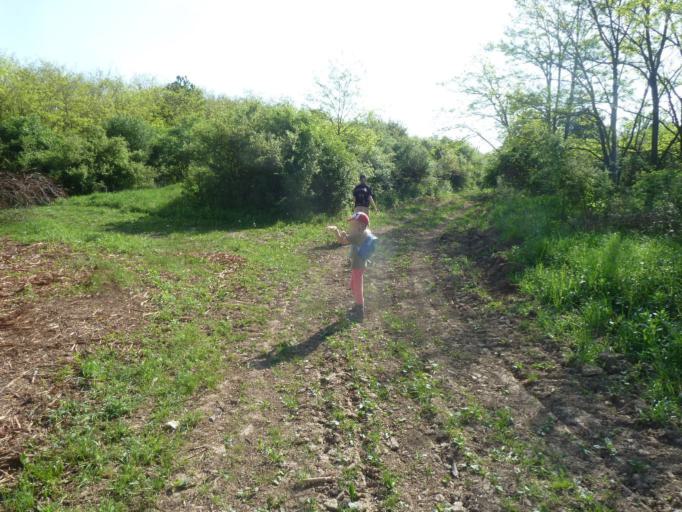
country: HU
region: Borsod-Abauj-Zemplen
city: Encs
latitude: 48.4233
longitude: 20.9951
